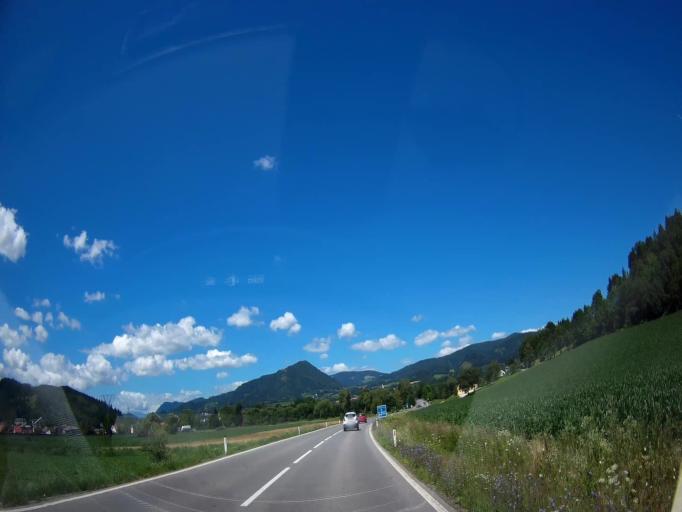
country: AT
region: Carinthia
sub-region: Politischer Bezirk Sankt Veit an der Glan
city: Sankt Veit an der Glan
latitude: 46.7636
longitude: 14.3859
